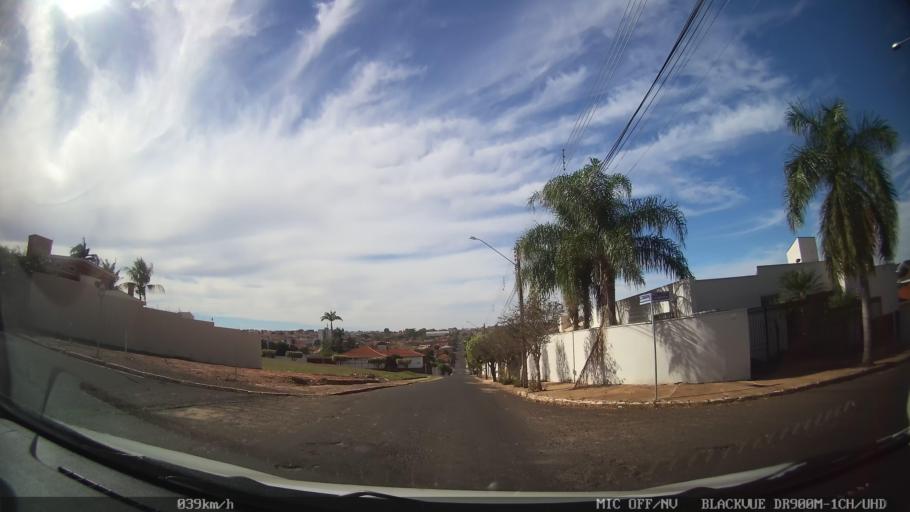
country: BR
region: Sao Paulo
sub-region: Catanduva
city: Catanduva
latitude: -21.1276
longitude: -48.9634
